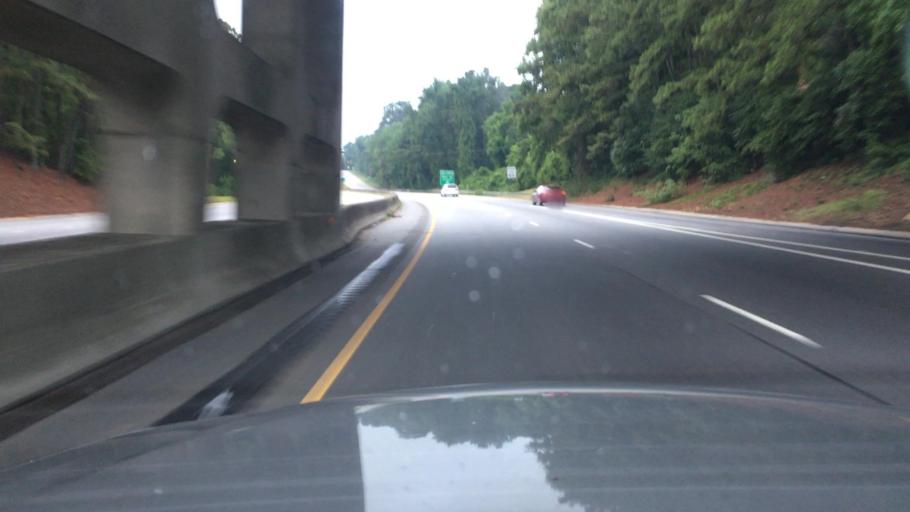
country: US
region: North Carolina
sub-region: Cumberland County
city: Fayetteville
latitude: 35.0610
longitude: -78.8918
